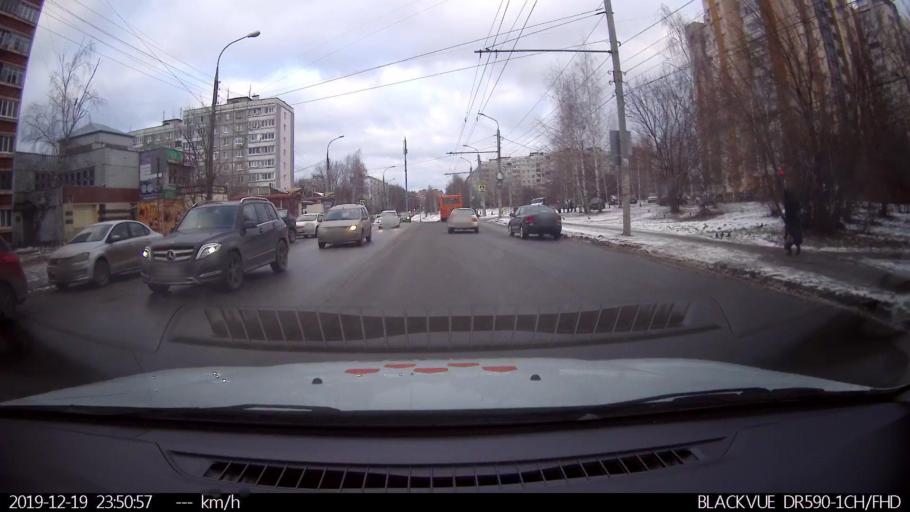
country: RU
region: Vologda
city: Lipin Bor
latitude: 60.9939
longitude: 37.9624
